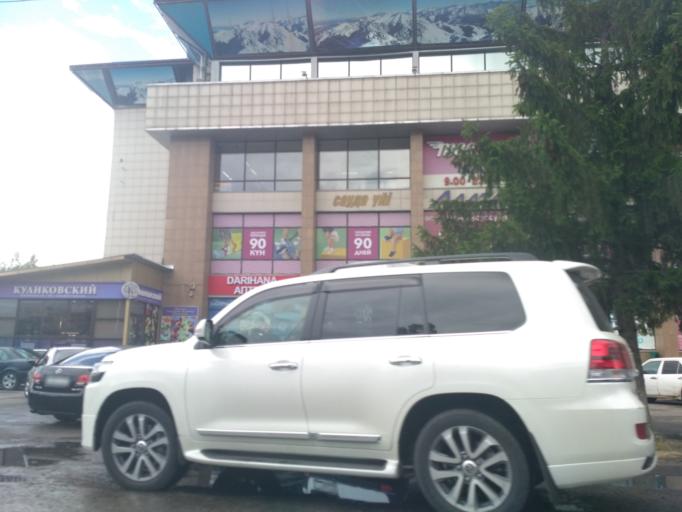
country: KZ
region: Almaty Oblysy
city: Burunday
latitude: 43.2031
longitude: 76.6198
